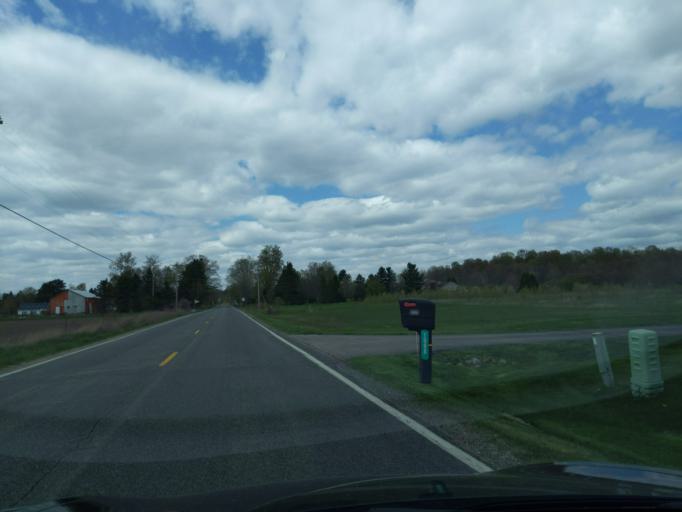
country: US
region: Michigan
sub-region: Ingham County
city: Mason
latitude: 42.6283
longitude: -84.4574
